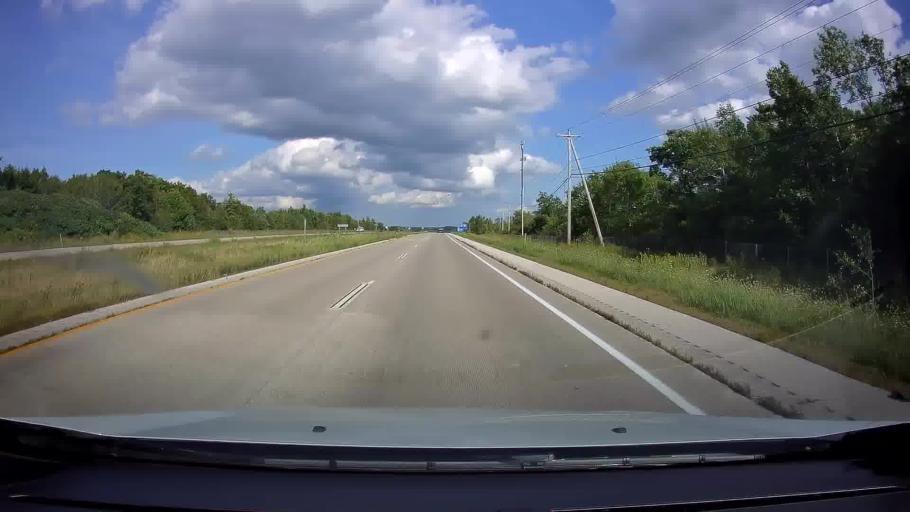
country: US
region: Wisconsin
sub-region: Kewaunee County
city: Luxemburg
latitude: 44.6335
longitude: -87.7953
